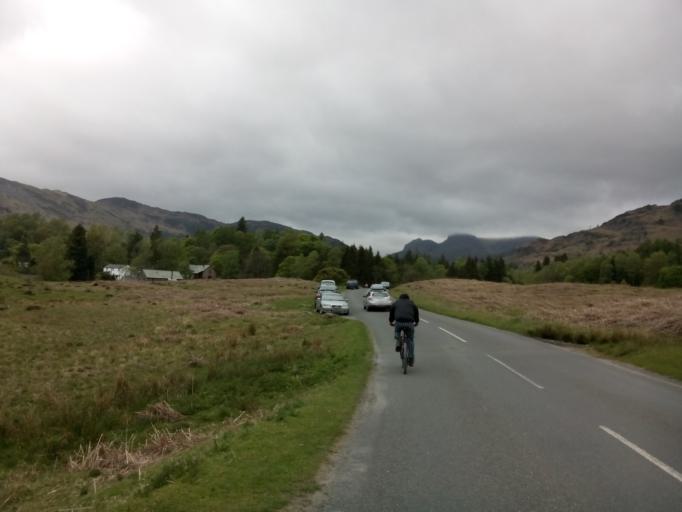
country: GB
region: England
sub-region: Cumbria
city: Ambleside
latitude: 54.4353
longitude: -3.0328
